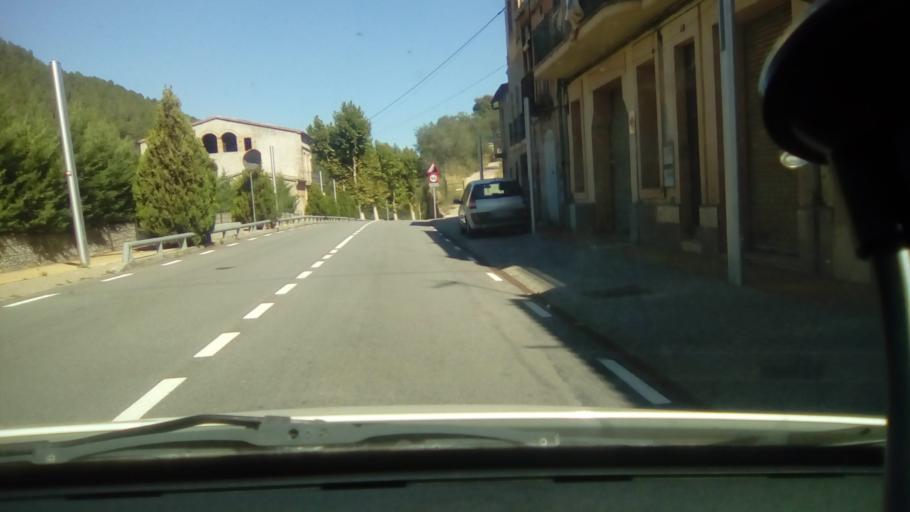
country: ES
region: Catalonia
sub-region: Provincia de Barcelona
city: Monistrol de Montserrat
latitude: 41.6367
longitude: 1.8541
